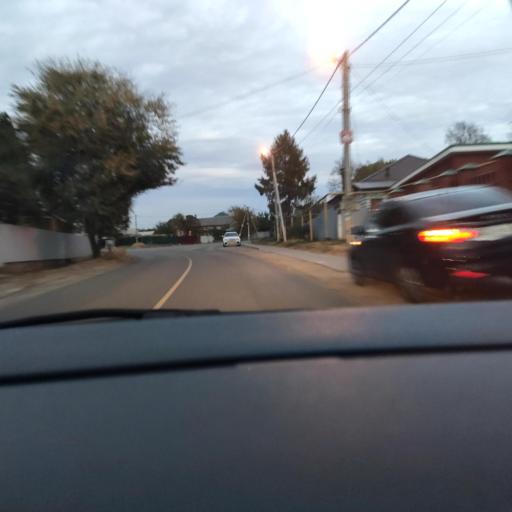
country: RU
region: Voronezj
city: Podgornoye
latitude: 51.7321
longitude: 39.1431
